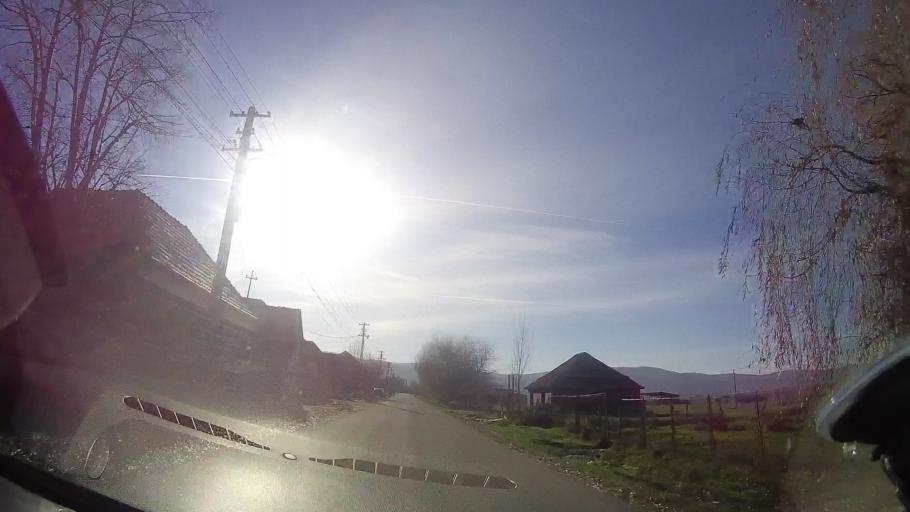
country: RO
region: Bihor
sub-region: Comuna Magesti
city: Magesti
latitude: 47.0206
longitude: 22.4693
